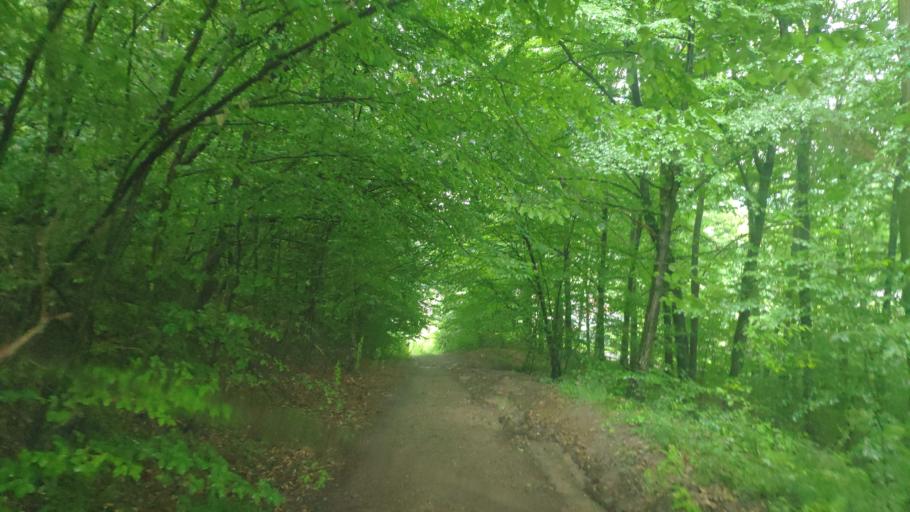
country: SK
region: Presovsky
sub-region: Okres Presov
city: Presov
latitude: 48.8634
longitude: 21.2162
